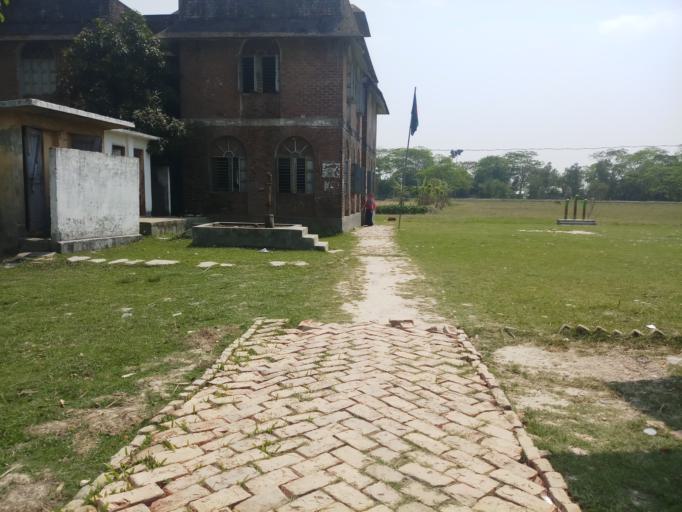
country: BD
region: Barisal
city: Mathba
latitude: 22.0420
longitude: 90.2842
